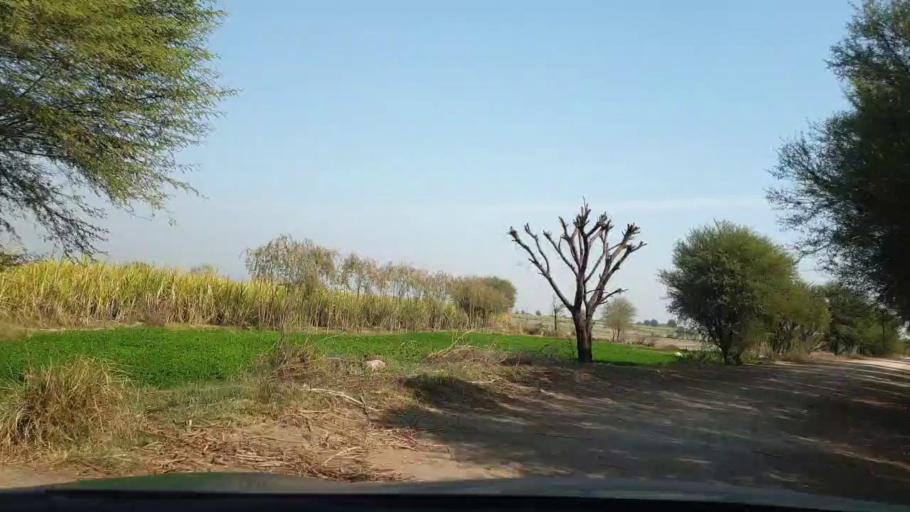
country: PK
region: Sindh
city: Berani
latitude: 25.7054
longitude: 68.7599
